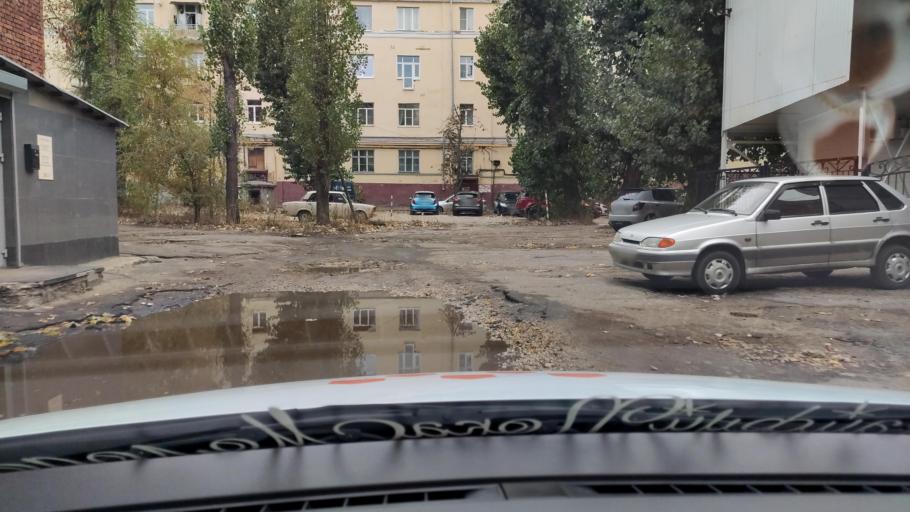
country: RU
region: Voronezj
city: Voronezh
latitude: 51.6819
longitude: 39.1897
